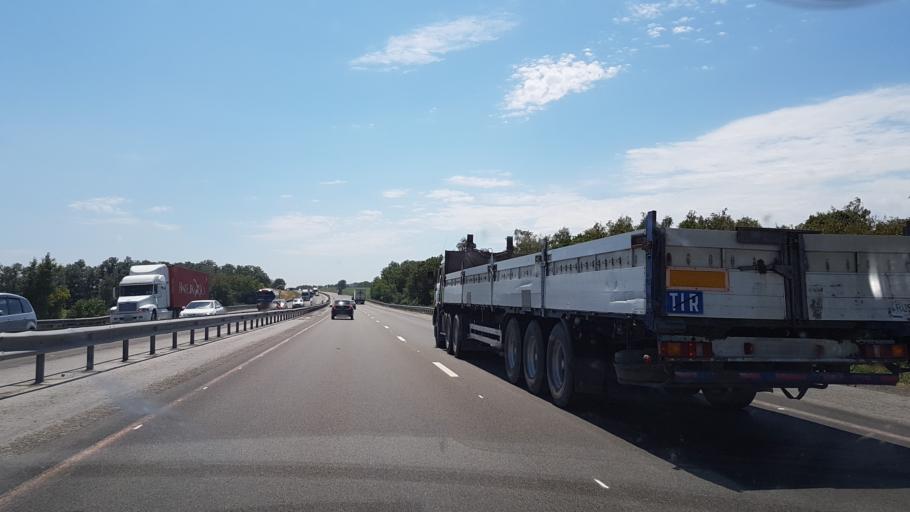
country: RU
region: Rostov
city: Krasyukovskaya
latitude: 47.5829
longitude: 39.9742
